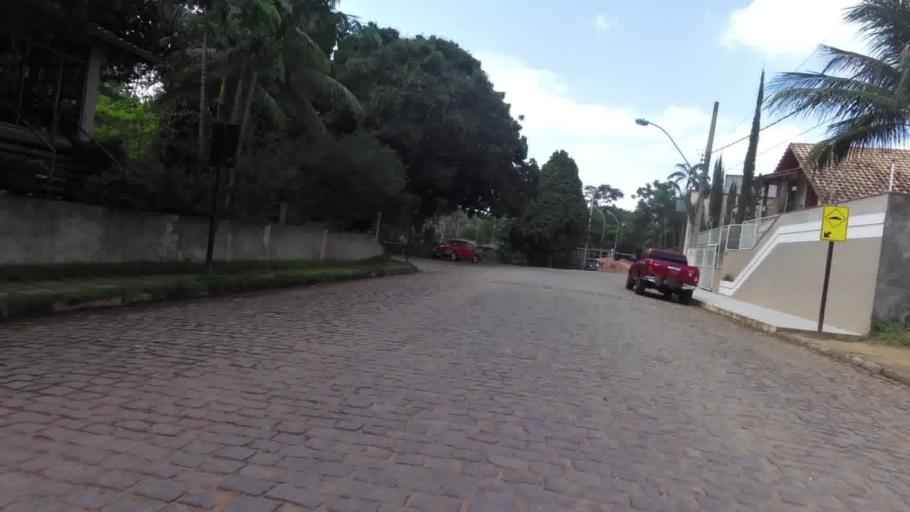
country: BR
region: Espirito Santo
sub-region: Alfredo Chaves
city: Alfredo Chaves
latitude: -20.6362
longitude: -40.7463
